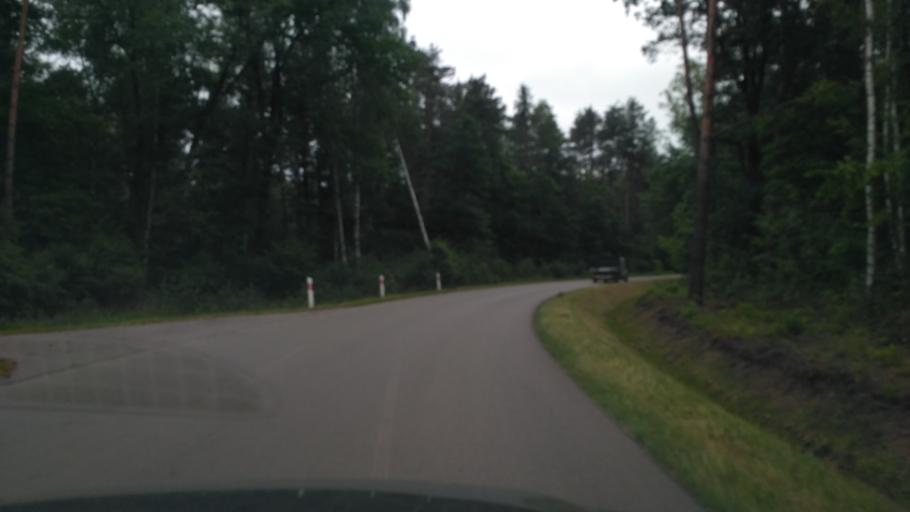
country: PL
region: Subcarpathian Voivodeship
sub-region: Powiat kolbuszowski
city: Niwiska
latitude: 50.1823
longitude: 21.6569
